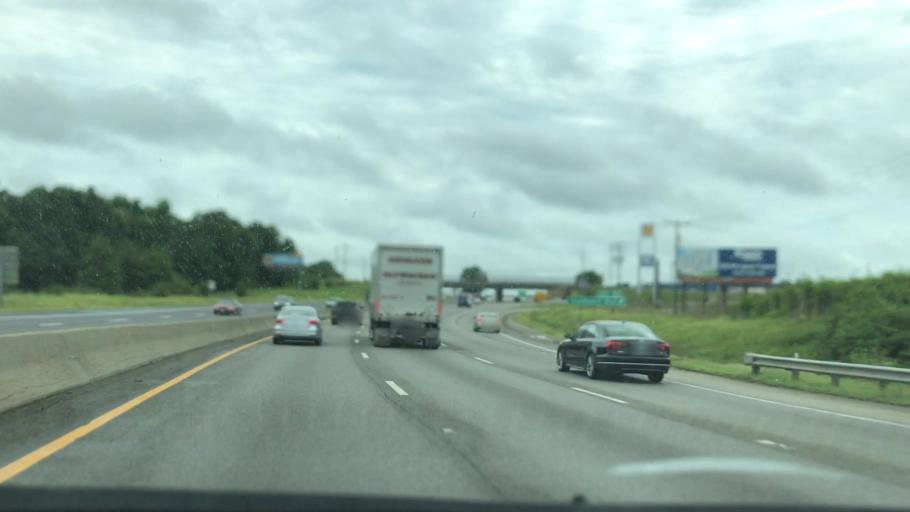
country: US
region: Virginia
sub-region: City of Petersburg
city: Petersburg
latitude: 37.2404
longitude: -77.3952
